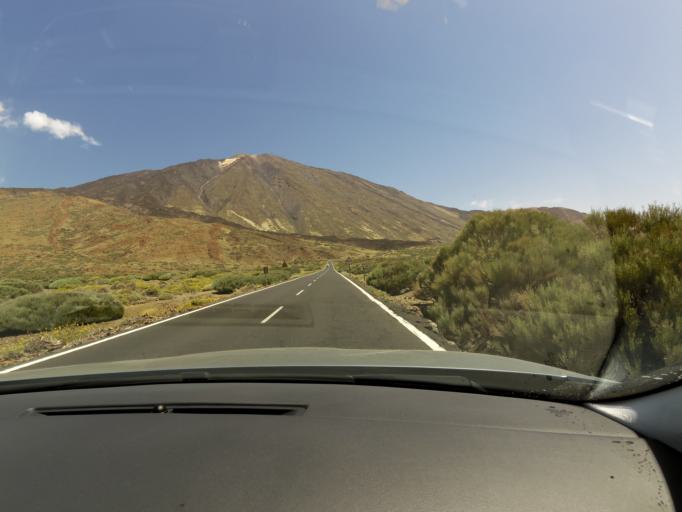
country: ES
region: Canary Islands
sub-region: Provincia de Santa Cruz de Tenerife
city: Vilaflor
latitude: 28.2382
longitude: -16.6298
